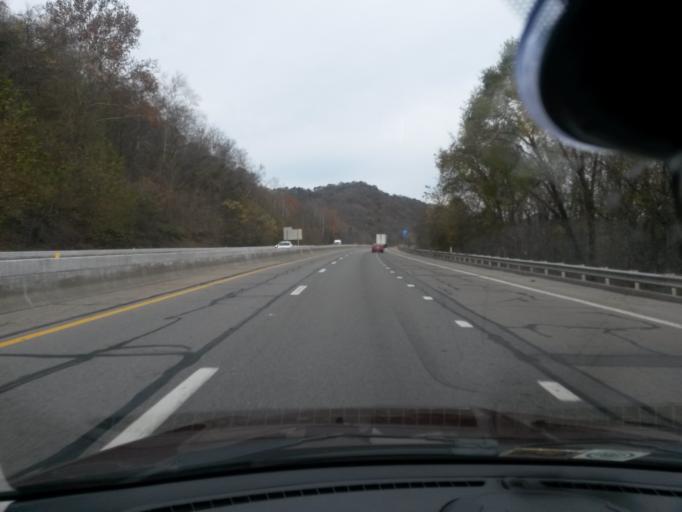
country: US
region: West Virginia
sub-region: Kanawha County
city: Marmet
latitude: 38.2437
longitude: -81.5687
